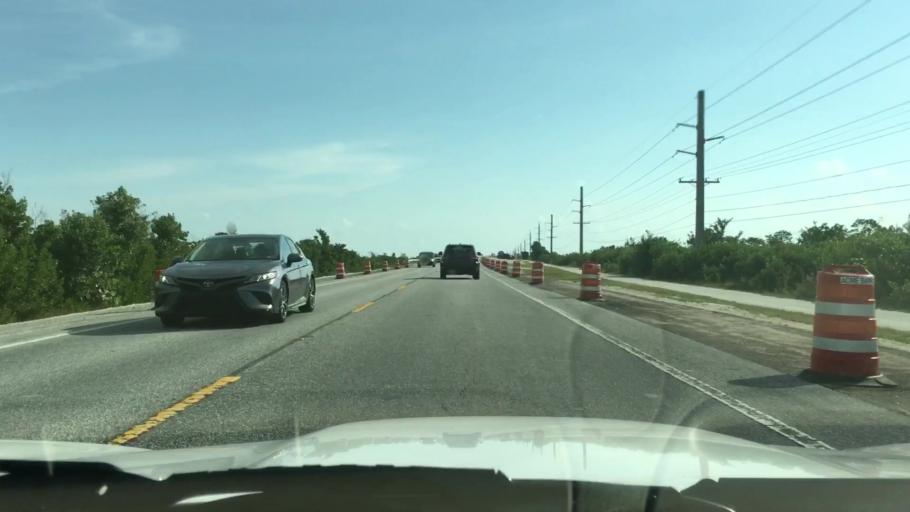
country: US
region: Florida
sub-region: Monroe County
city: Cudjoe Key
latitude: 24.6629
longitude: -81.4706
